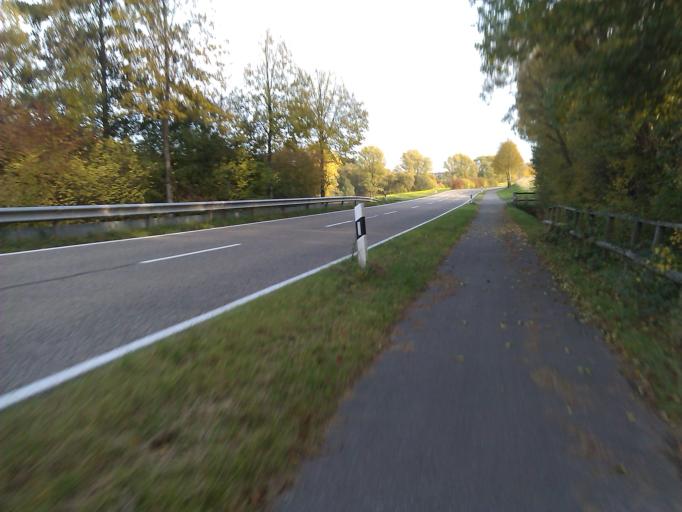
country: DE
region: Rheinland-Pfalz
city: Schallodenbach
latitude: 49.5515
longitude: 7.6994
